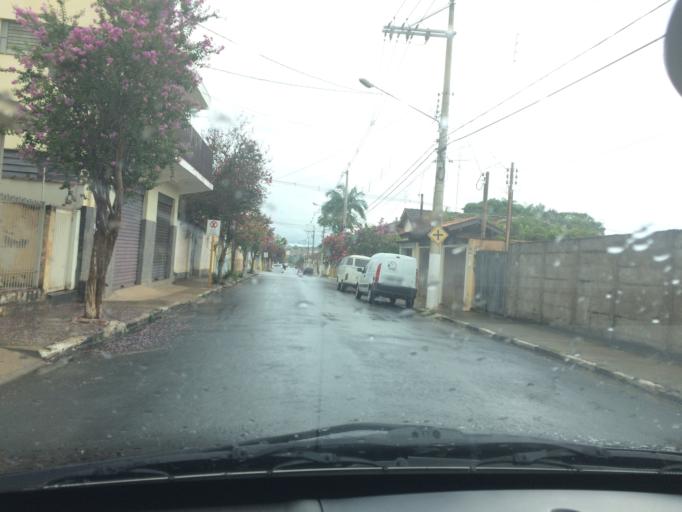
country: BR
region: Sao Paulo
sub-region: Casa Branca
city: Casa Branca
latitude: -21.7713
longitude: -47.0854
